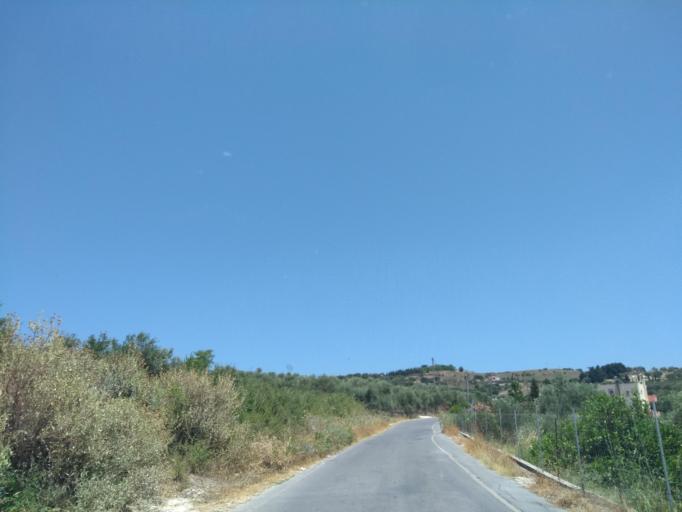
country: GR
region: Crete
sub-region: Nomos Chanias
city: Georgioupolis
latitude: 35.3254
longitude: 24.3260
